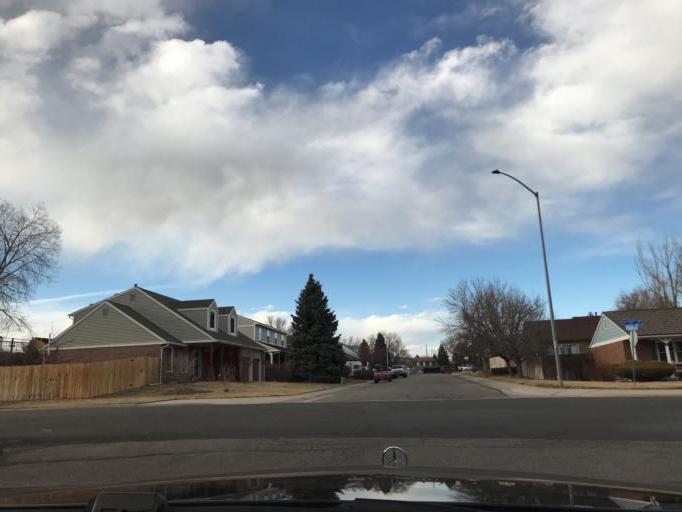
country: US
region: Colorado
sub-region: Jefferson County
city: Applewood
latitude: 39.8243
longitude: -105.1626
